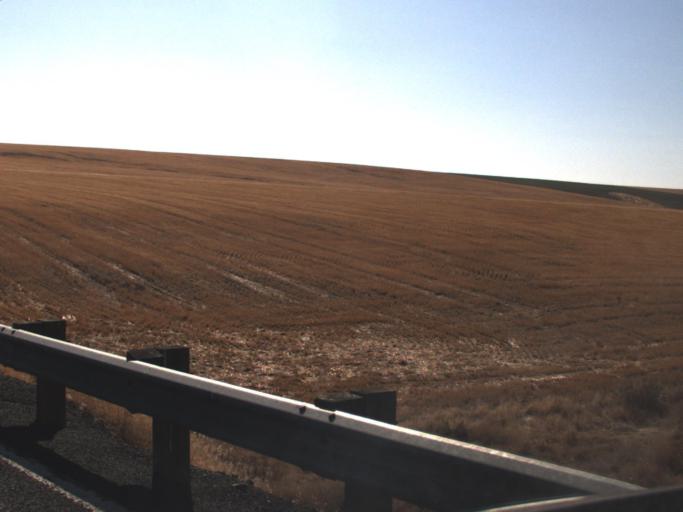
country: US
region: Washington
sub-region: Adams County
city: Ritzville
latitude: 47.0827
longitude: -118.6639
